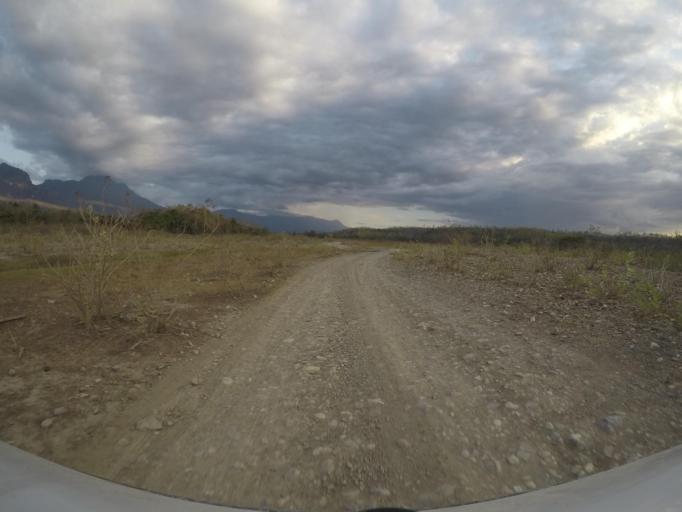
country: TL
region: Bobonaro
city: Maliana
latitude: -8.8943
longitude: 125.2086
